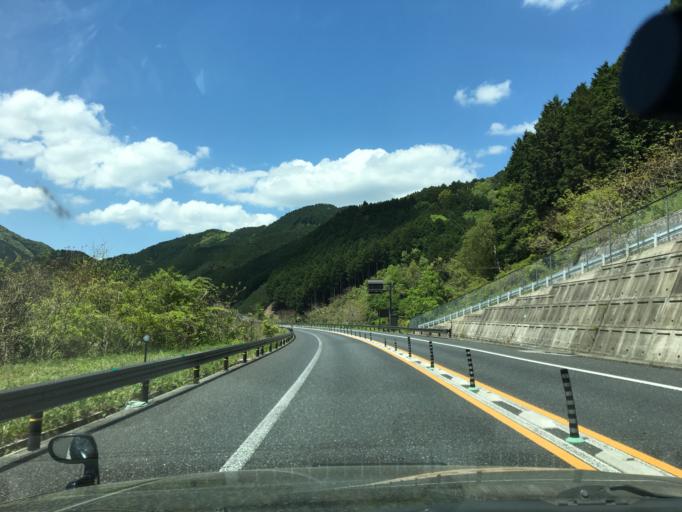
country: JP
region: Kyoto
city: Fukuchiyama
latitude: 35.2894
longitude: 134.9751
